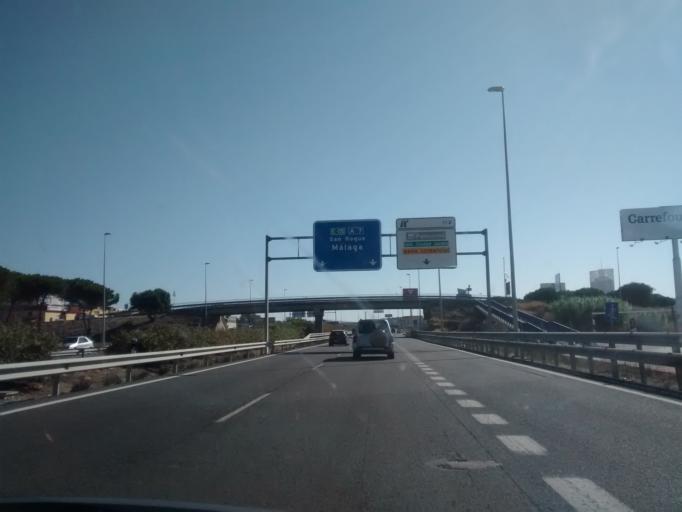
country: ES
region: Andalusia
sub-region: Provincia de Cadiz
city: Algeciras
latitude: 36.1821
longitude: -5.4426
